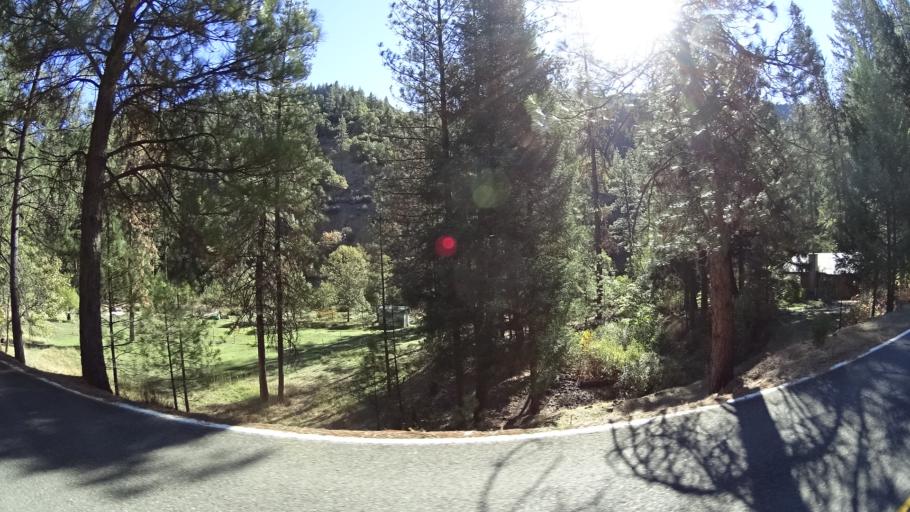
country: US
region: California
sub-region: Trinity County
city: Weaverville
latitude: 41.1643
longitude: -123.0943
